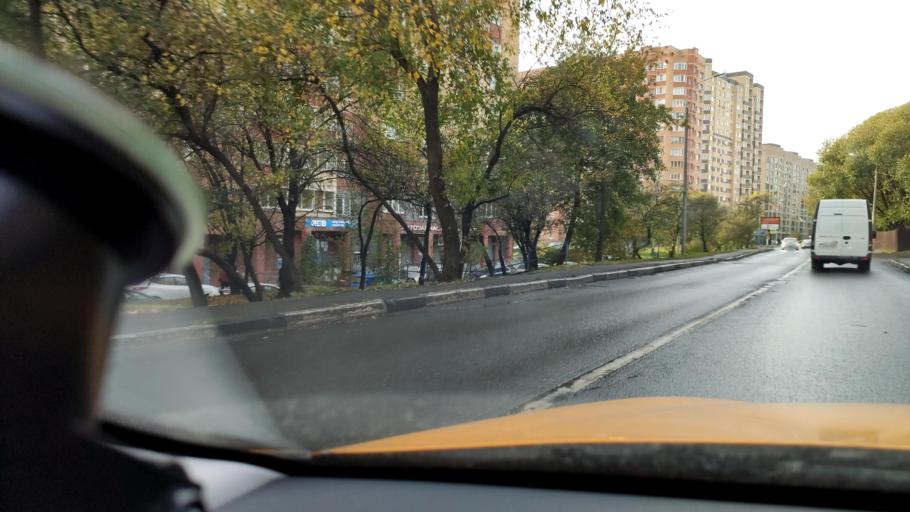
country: RU
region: Moskovskaya
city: Mytishchi
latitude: 55.9186
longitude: 37.7304
